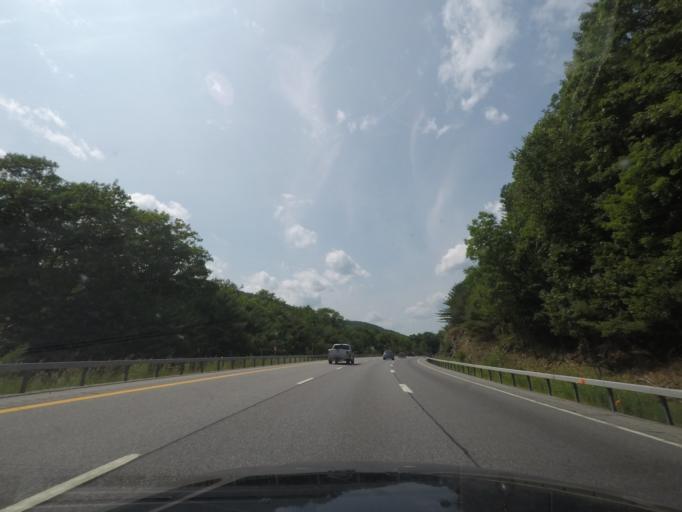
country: US
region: New York
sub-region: Warren County
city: Warrensburg
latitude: 43.4614
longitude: -73.7410
